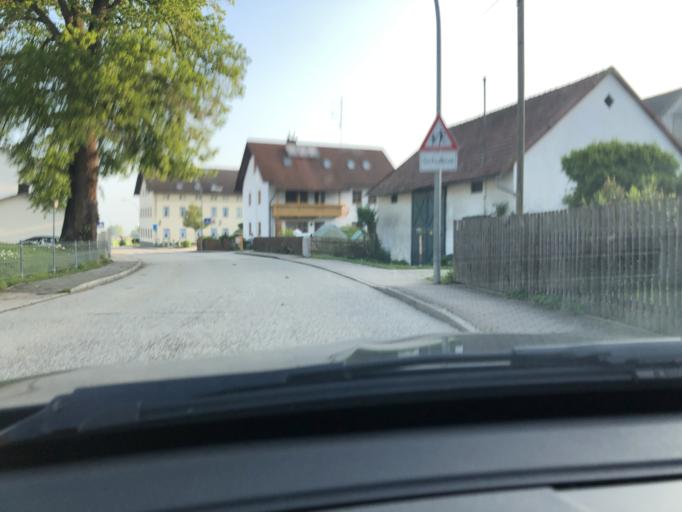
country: DE
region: Bavaria
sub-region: Upper Bavaria
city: Freising
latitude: 48.4396
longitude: 11.7237
